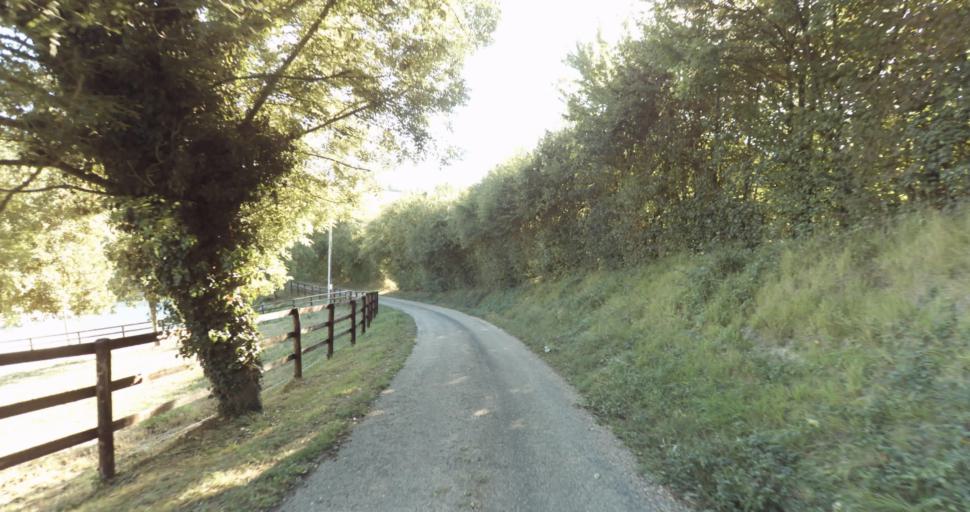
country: FR
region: Lower Normandy
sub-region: Departement de l'Orne
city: Vimoutiers
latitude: 48.8970
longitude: 0.1441
